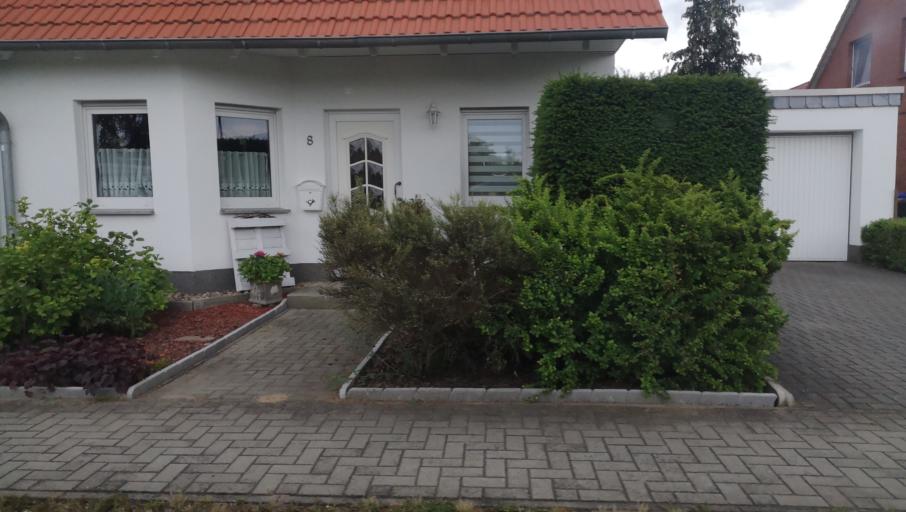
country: DE
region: Saxony-Anhalt
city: Barleben
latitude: 52.2110
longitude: 11.6130
